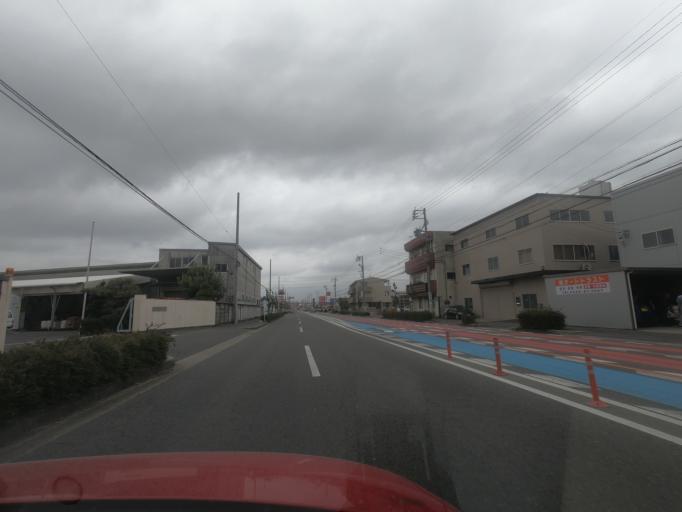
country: JP
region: Aichi
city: Kasugai
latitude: 35.2605
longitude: 136.9666
